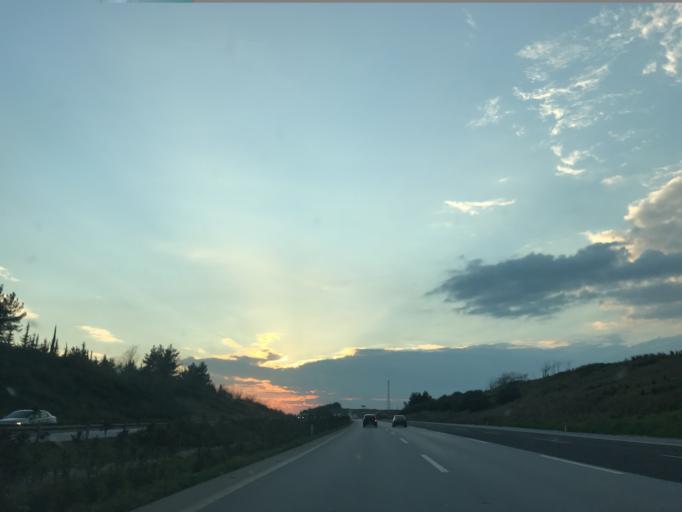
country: TR
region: Mersin
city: Yenice
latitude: 37.0199
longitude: 35.0162
